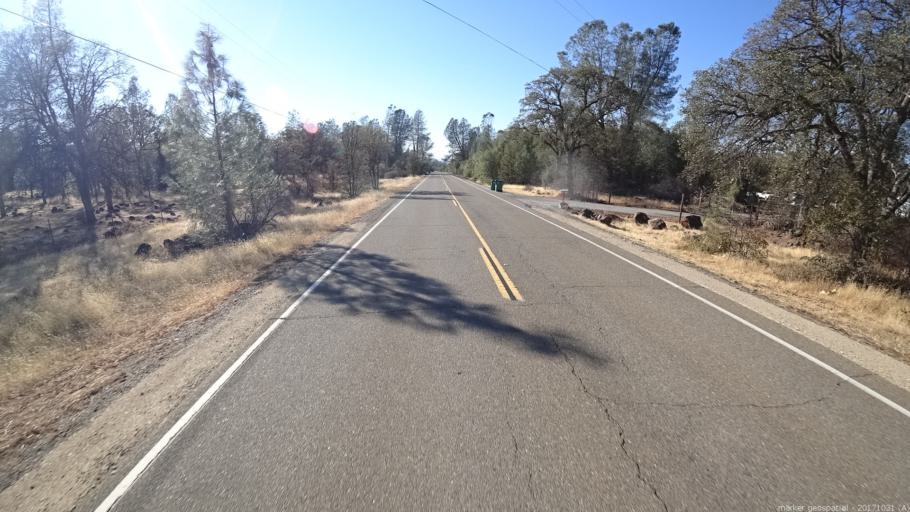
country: US
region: California
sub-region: Shasta County
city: Shingletown
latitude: 40.4898
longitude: -122.0615
